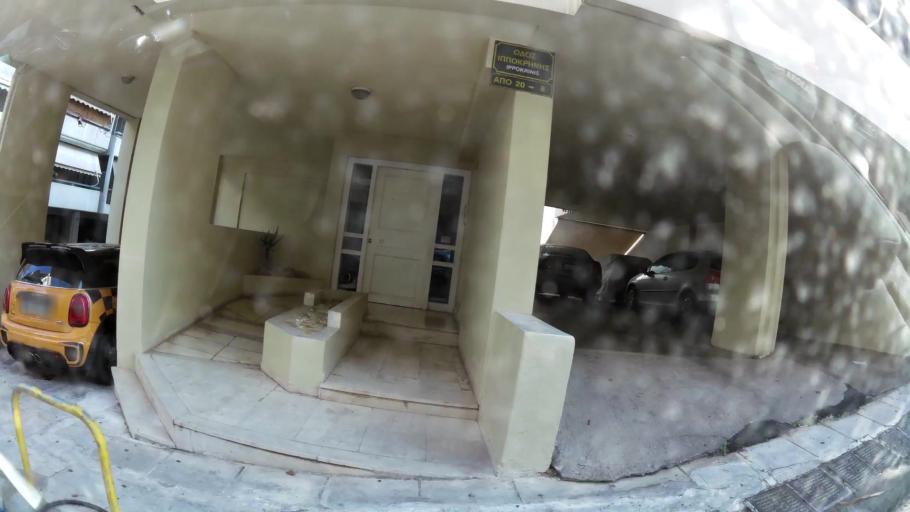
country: GR
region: Attica
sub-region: Nomarchia Athinas
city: Kaisariani
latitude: 37.9801
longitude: 23.7704
